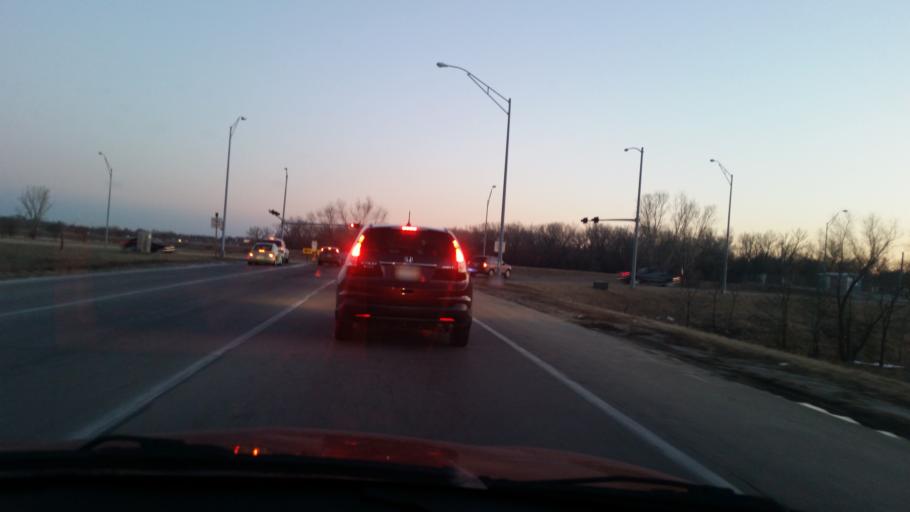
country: US
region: Nebraska
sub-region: Sarpy County
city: Offutt Air Force Base
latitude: 41.1407
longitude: -95.9404
